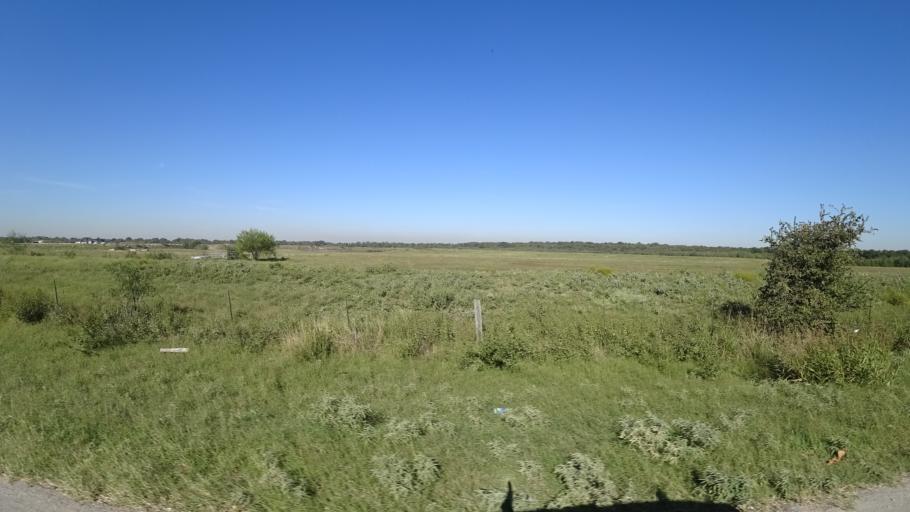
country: US
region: Texas
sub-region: Travis County
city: Hornsby Bend
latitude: 30.2519
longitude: -97.6151
